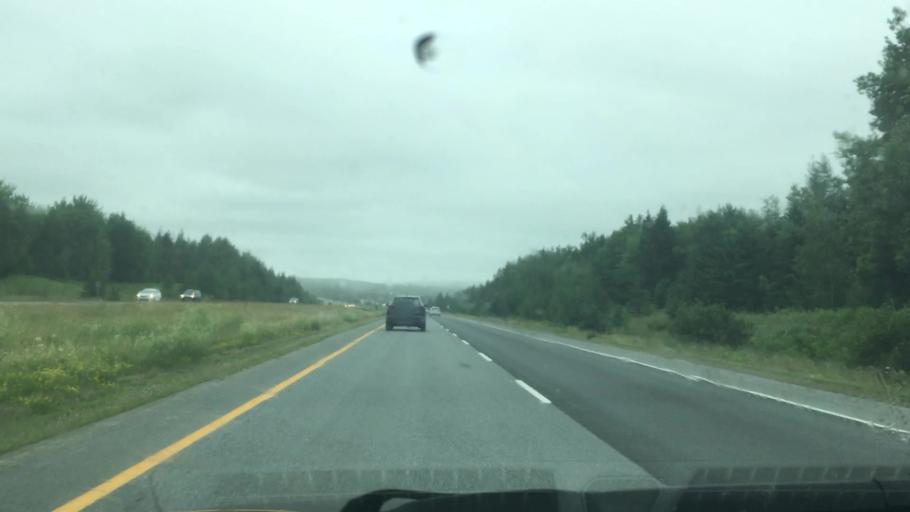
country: CA
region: Nova Scotia
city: Truro
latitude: 45.2407
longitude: -63.2932
